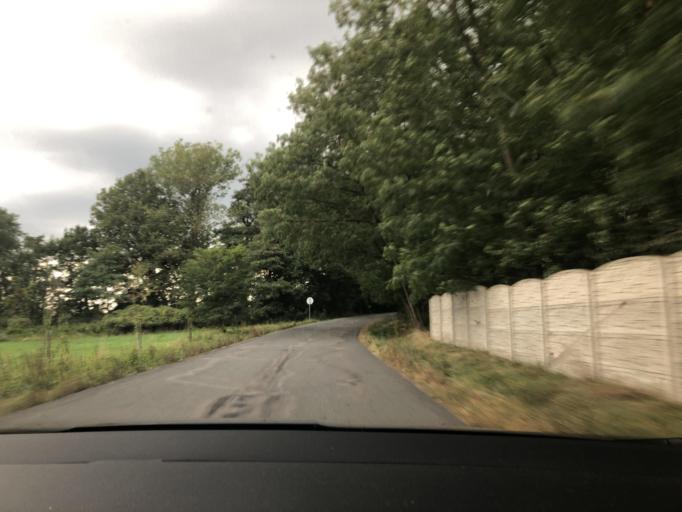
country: CZ
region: Pardubicky
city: Chvaletice
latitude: 50.0519
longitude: 15.3932
